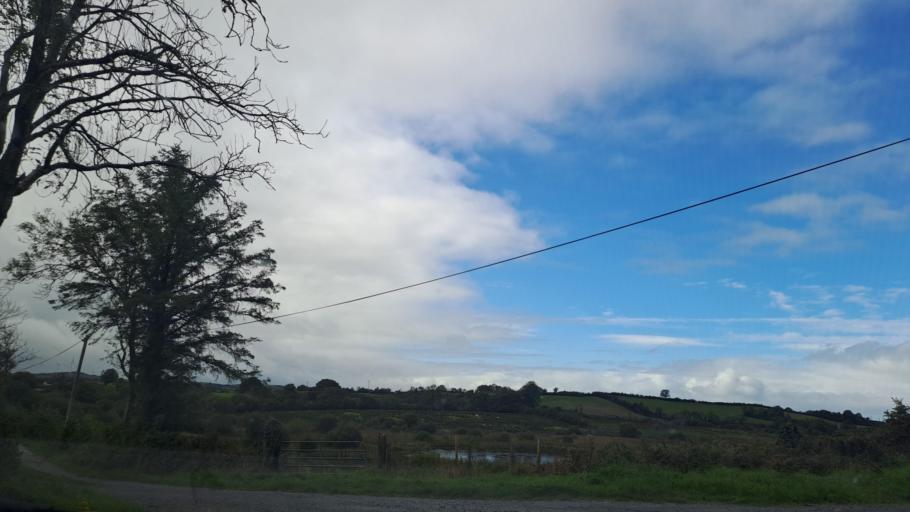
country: IE
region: Ulster
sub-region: An Cabhan
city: Kingscourt
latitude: 53.9853
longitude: -6.8323
